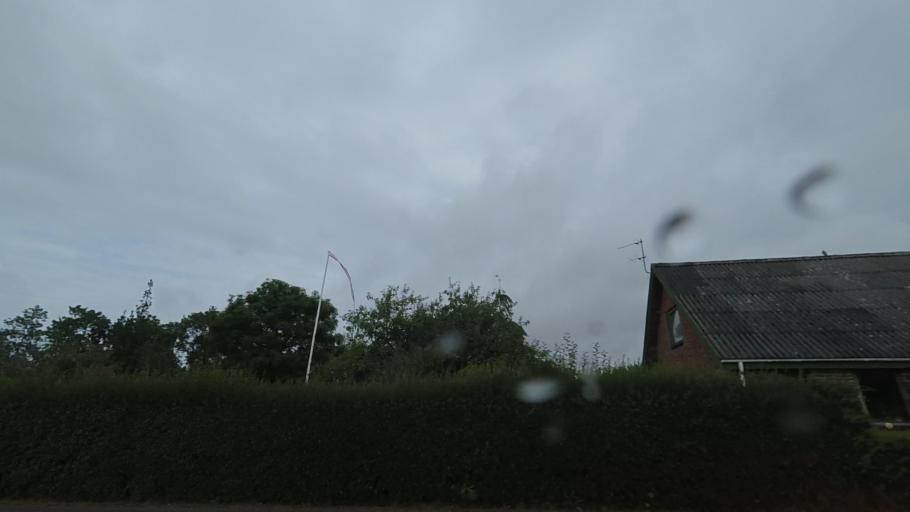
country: DK
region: Central Jutland
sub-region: Syddjurs Kommune
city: Ronde
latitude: 56.3111
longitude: 10.4616
